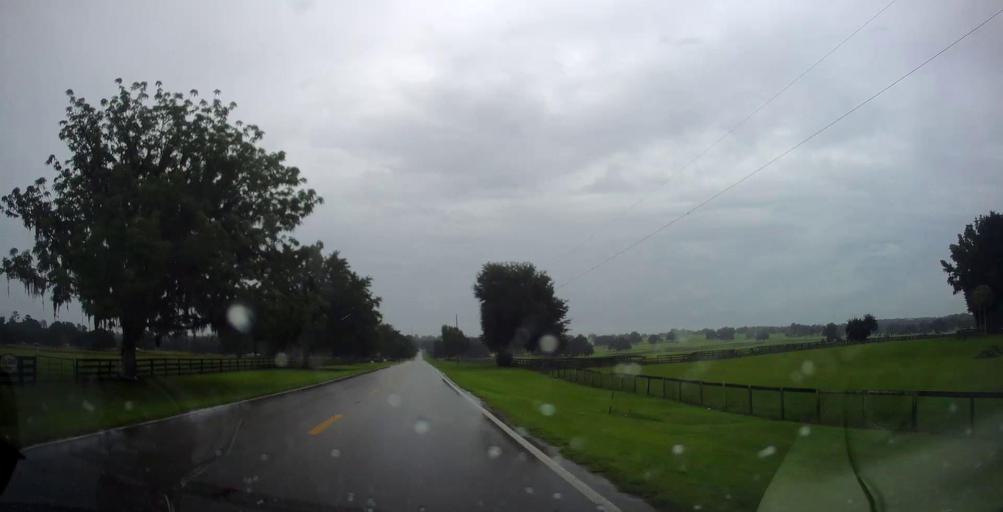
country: US
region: Florida
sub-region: Marion County
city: Citra
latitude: 29.3574
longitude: -82.2426
